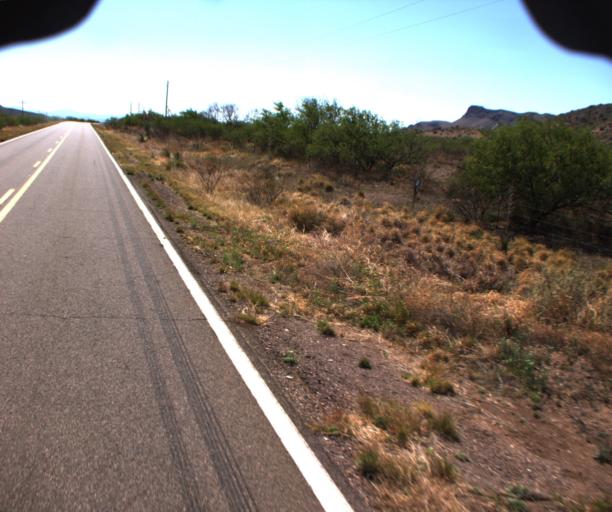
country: US
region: Arizona
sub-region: Cochise County
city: Douglas
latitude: 31.4869
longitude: -109.4171
